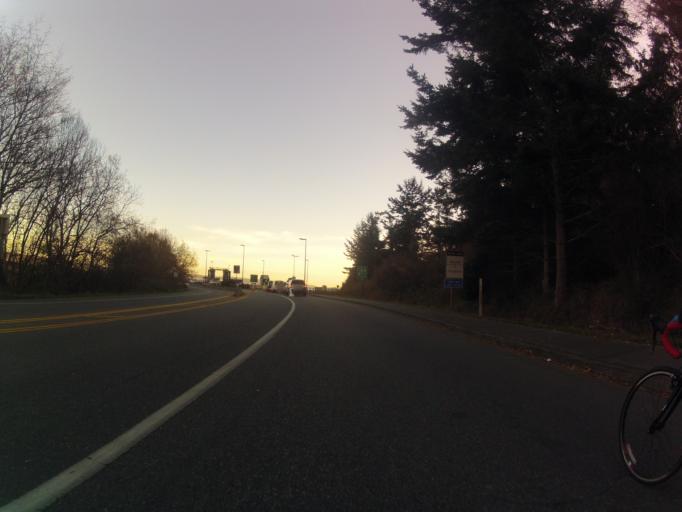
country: US
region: Washington
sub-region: Island County
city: Coupeville
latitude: 48.1609
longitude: -122.6746
